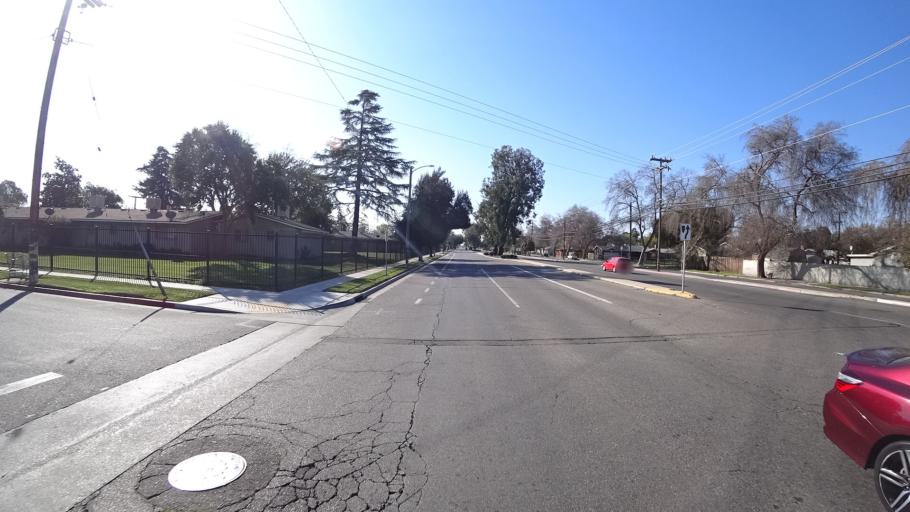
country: US
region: California
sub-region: Fresno County
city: Fresno
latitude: 36.7252
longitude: -119.7364
